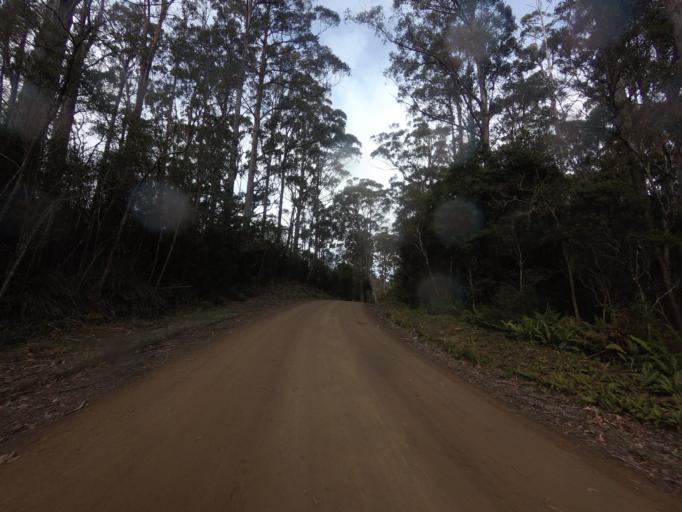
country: AU
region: Tasmania
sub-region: Huon Valley
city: Geeveston
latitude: -43.5440
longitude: 146.8901
